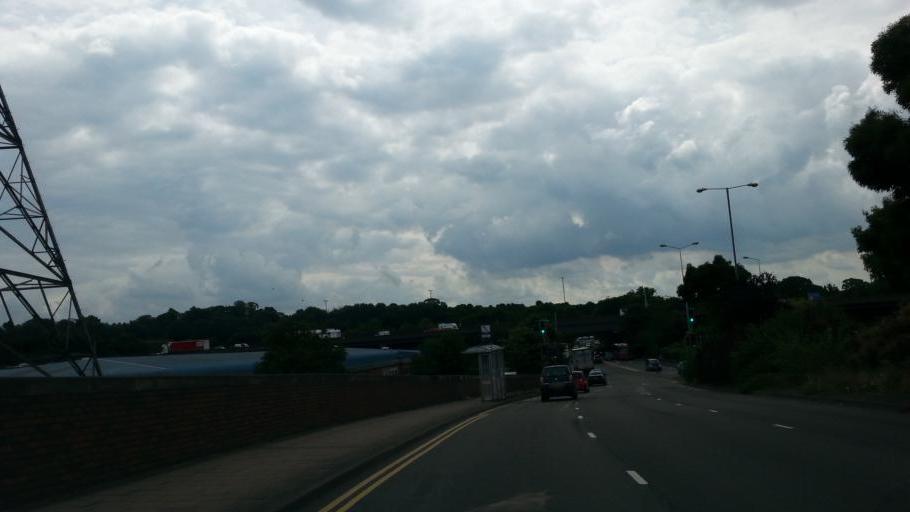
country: GB
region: England
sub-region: Warwickshire
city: Water Orton
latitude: 52.5111
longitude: -1.7970
